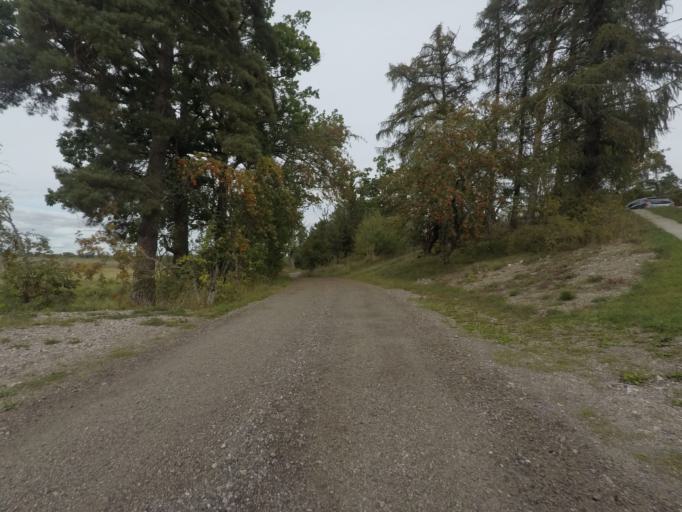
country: SE
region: Vaestmanland
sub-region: Kungsors Kommun
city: Kungsoer
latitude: 59.4620
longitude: 16.0708
